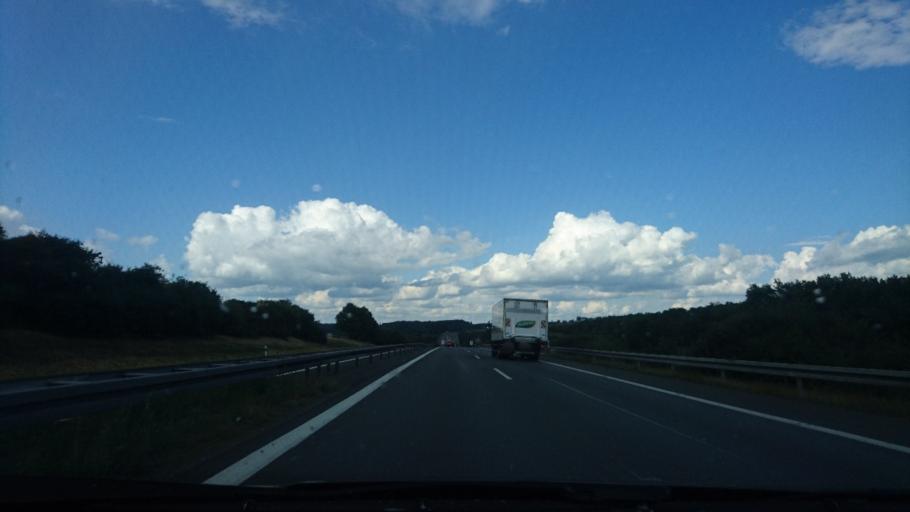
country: DE
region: Saxony
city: Neuensalz
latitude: 50.4797
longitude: 12.1853
